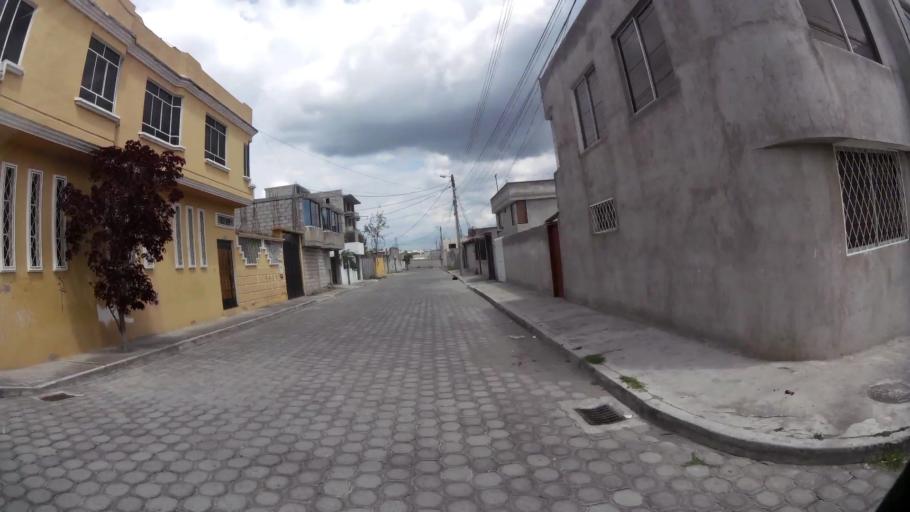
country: EC
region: Pichincha
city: Quito
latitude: -0.0825
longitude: -78.4120
